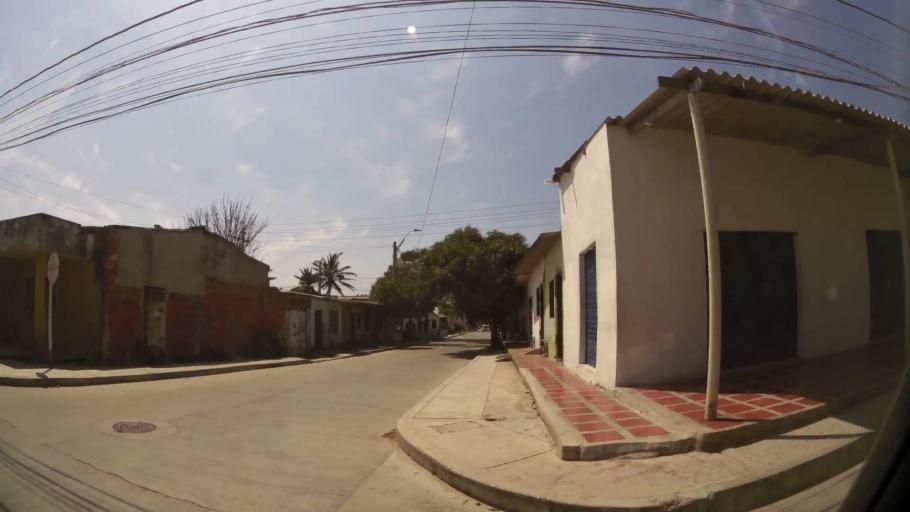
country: CO
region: Atlantico
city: Barranquilla
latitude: 10.9754
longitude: -74.8320
